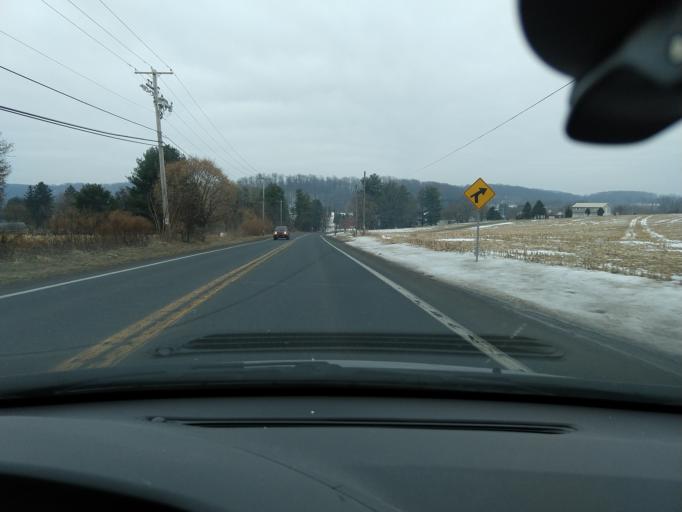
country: US
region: Pennsylvania
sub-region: Lehigh County
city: Macungie
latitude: 40.4859
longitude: -75.5235
